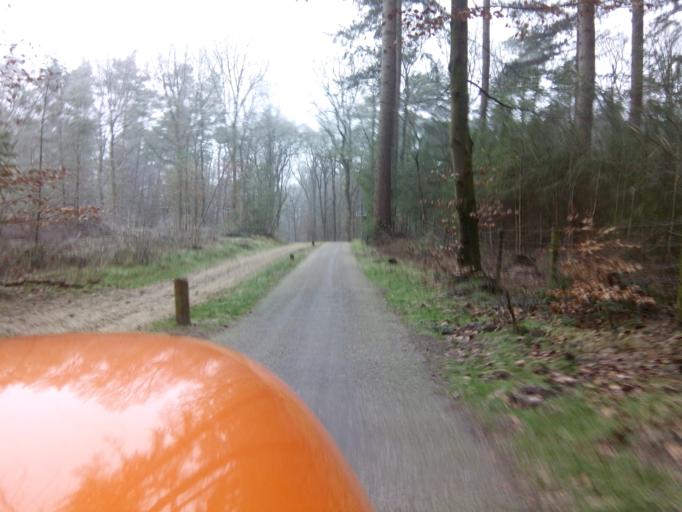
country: NL
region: Gelderland
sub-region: Gemeente Barneveld
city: Garderen
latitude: 52.2407
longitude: 5.7069
